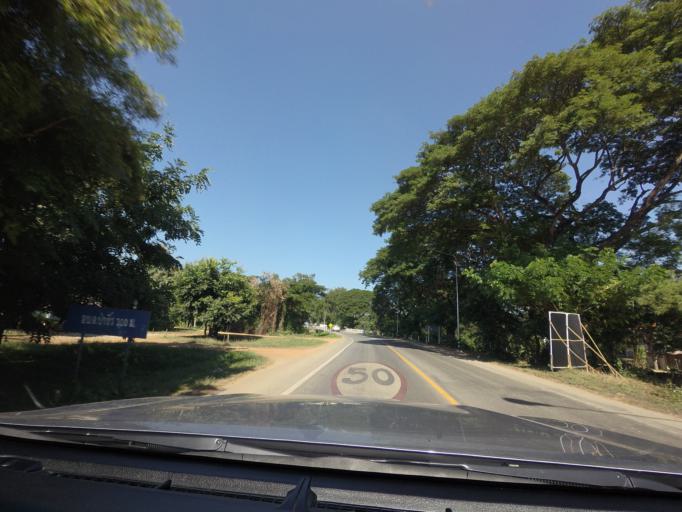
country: TH
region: Sukhothai
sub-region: Amphoe Si Satchanalai
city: Si Satchanalai
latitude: 17.5372
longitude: 99.7770
